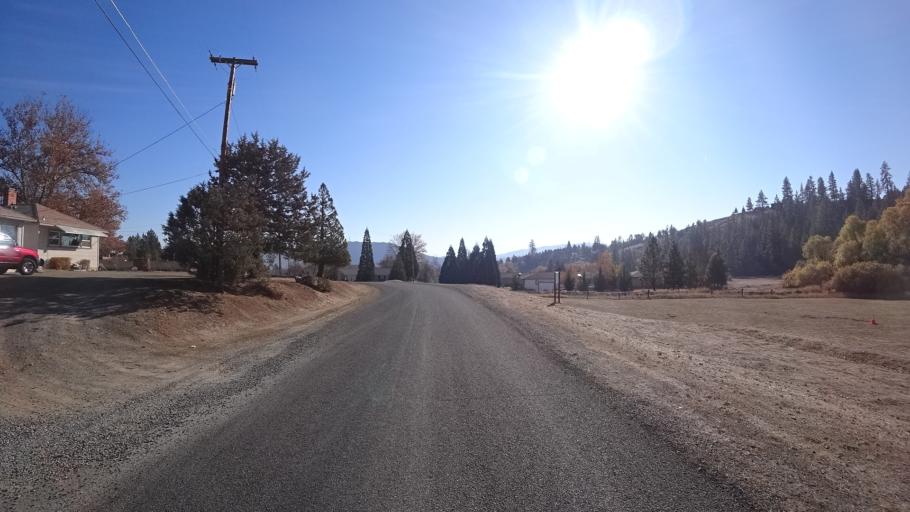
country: US
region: California
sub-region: Siskiyou County
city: Yreka
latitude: 41.7322
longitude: -122.6550
